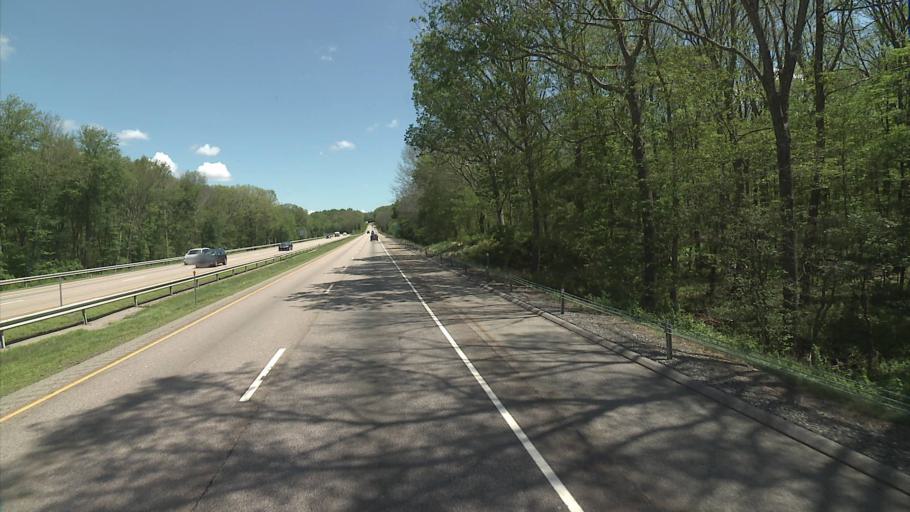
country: US
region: Connecticut
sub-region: New London County
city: Oxoboxo River
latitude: 41.4229
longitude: -72.1293
